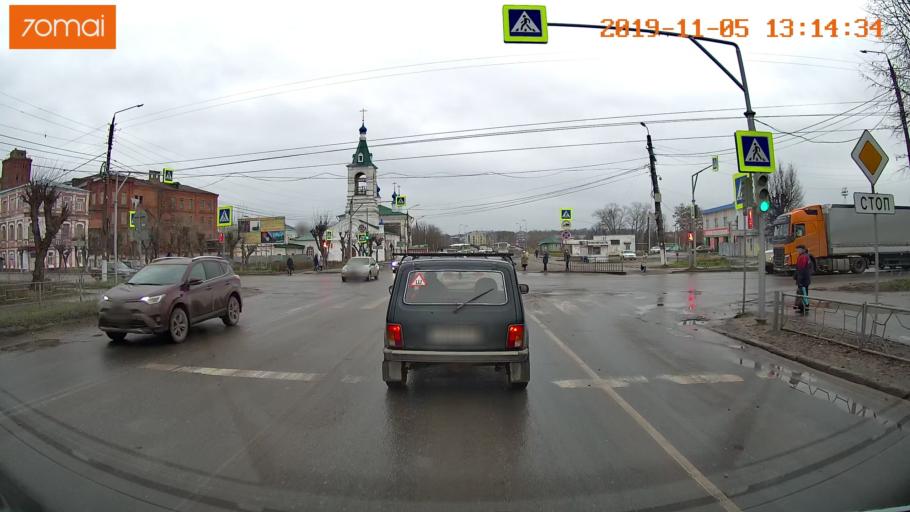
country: RU
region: Ivanovo
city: Shuya
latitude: 56.8511
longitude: 41.3571
